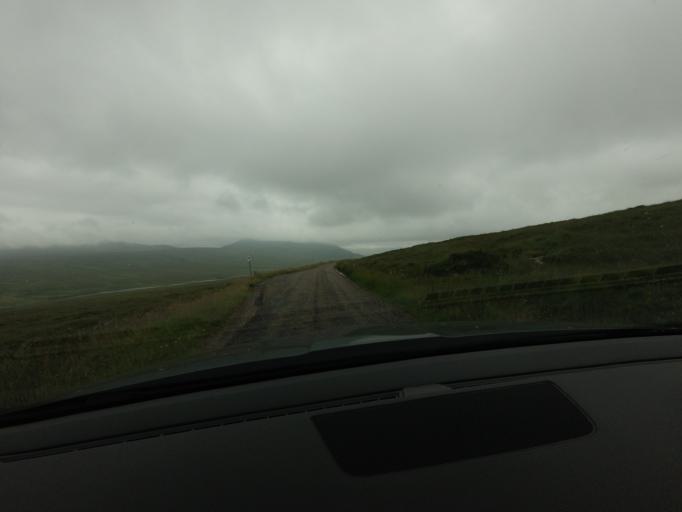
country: GB
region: Scotland
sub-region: Highland
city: Golspie
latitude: 58.3449
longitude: -4.4334
